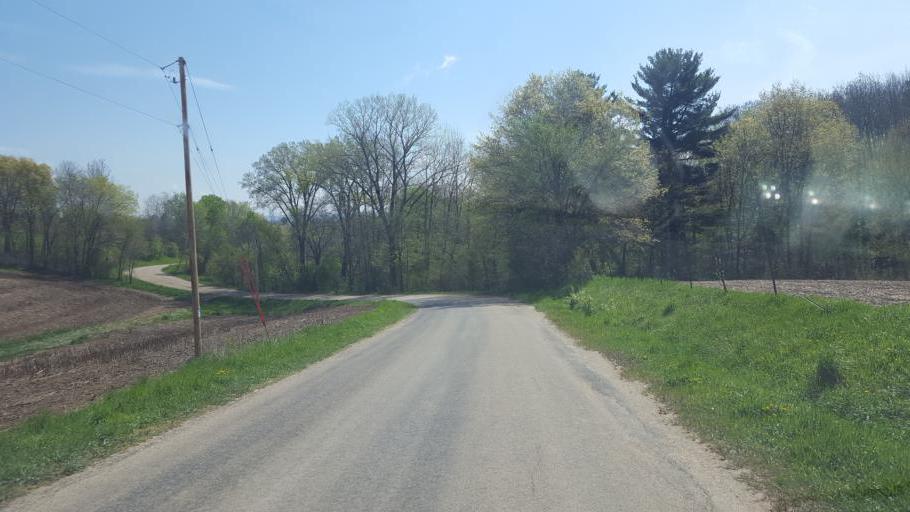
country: US
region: Wisconsin
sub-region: Vernon County
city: Hillsboro
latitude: 43.6944
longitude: -90.3075
